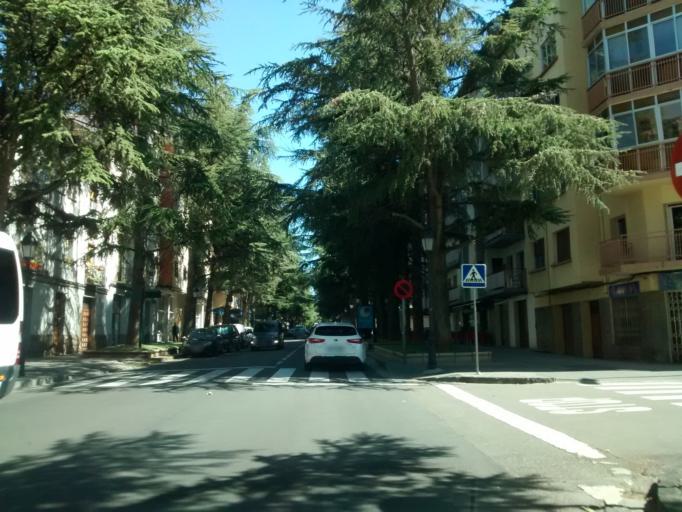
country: ES
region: Aragon
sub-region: Provincia de Huesca
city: Jaca
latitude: 42.5740
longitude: -0.5492
